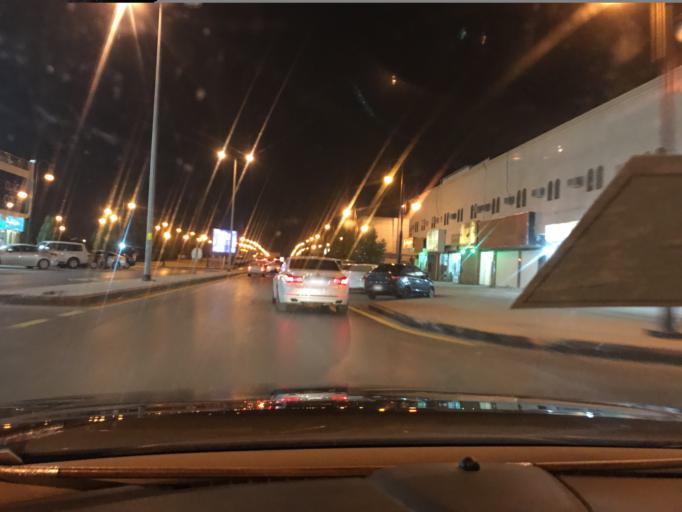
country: SA
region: Ar Riyad
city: Riyadh
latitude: 24.7437
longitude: 46.7650
